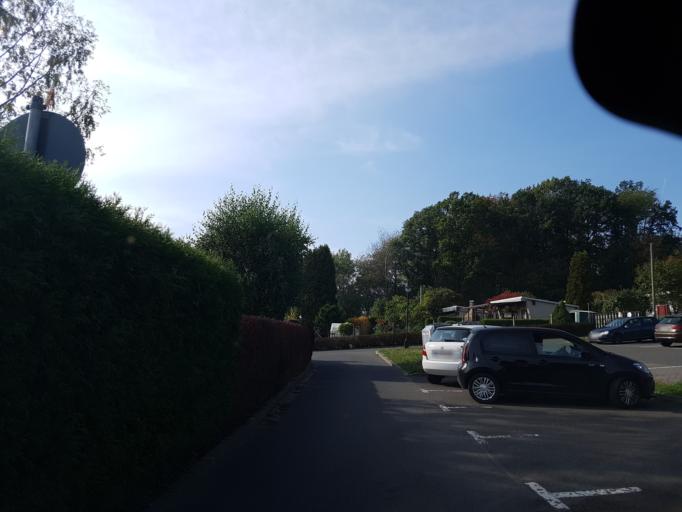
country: DE
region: Saxony
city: Hartha
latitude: 51.1017
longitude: 12.9631
